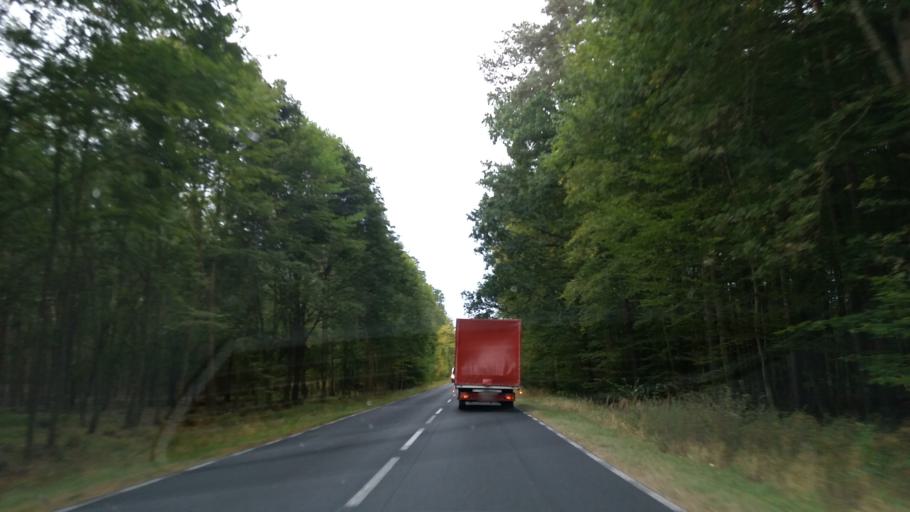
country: PL
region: West Pomeranian Voivodeship
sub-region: Powiat mysliborski
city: Barlinek
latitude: 52.9281
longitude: 15.1939
